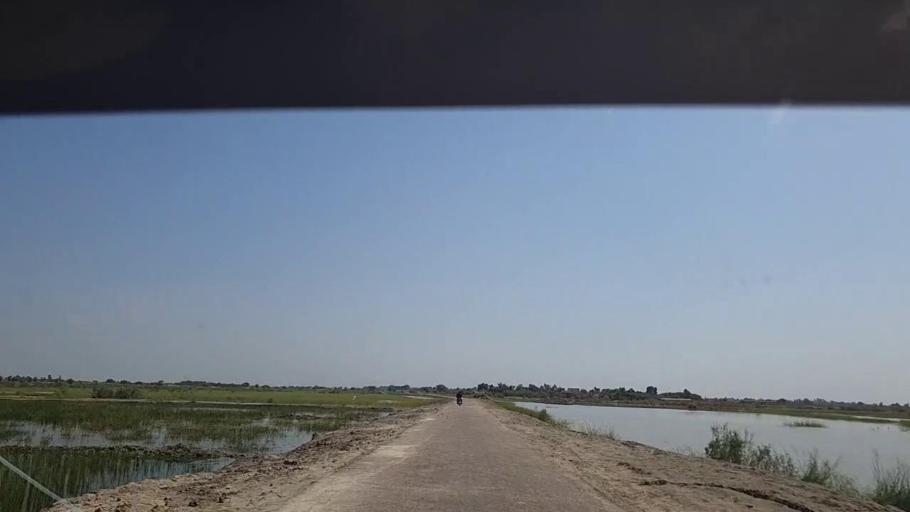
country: PK
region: Sindh
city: Kandhkot
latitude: 28.1758
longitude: 69.1595
